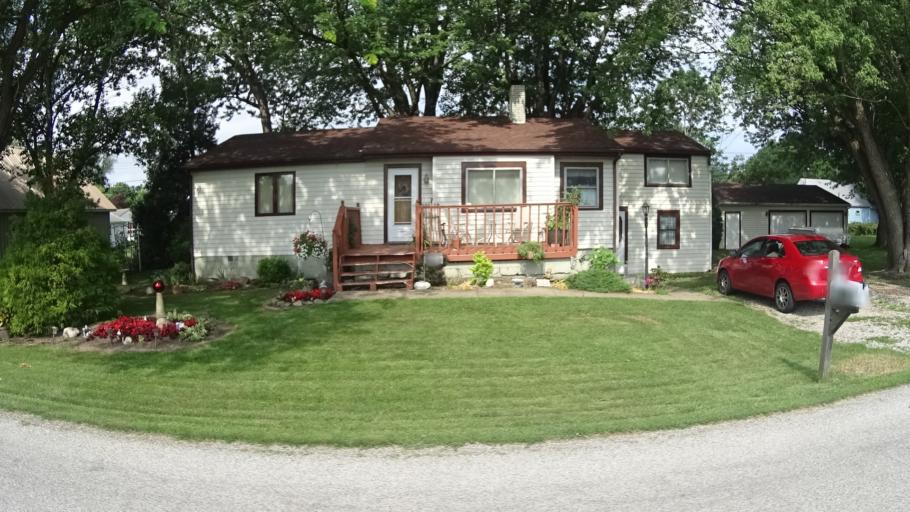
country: US
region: Ohio
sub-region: Lorain County
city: Vermilion
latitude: 41.4008
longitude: -82.4192
